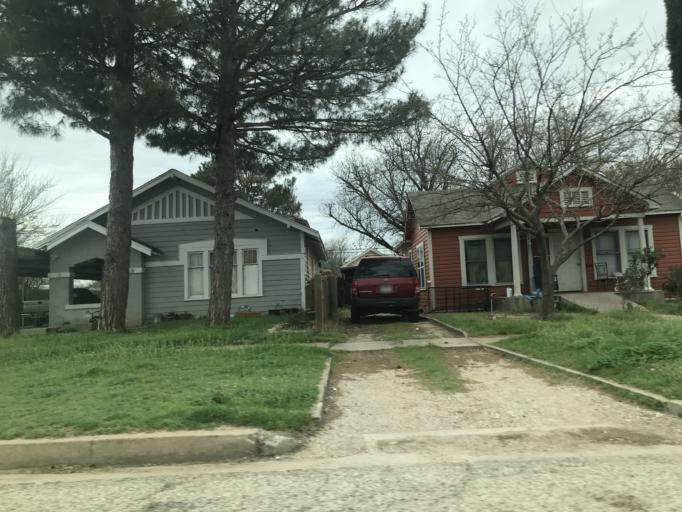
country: US
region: Texas
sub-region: Taylor County
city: Abilene
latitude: 32.4597
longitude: -99.7382
